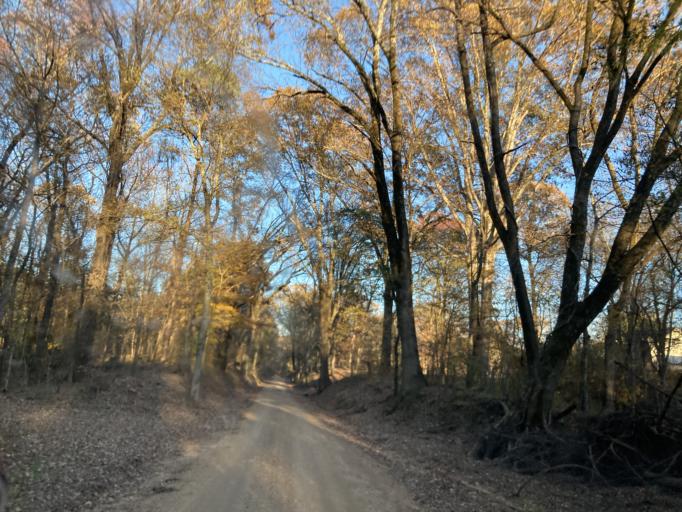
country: US
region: Mississippi
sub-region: Yazoo County
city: Yazoo City
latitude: 32.9495
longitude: -90.2752
